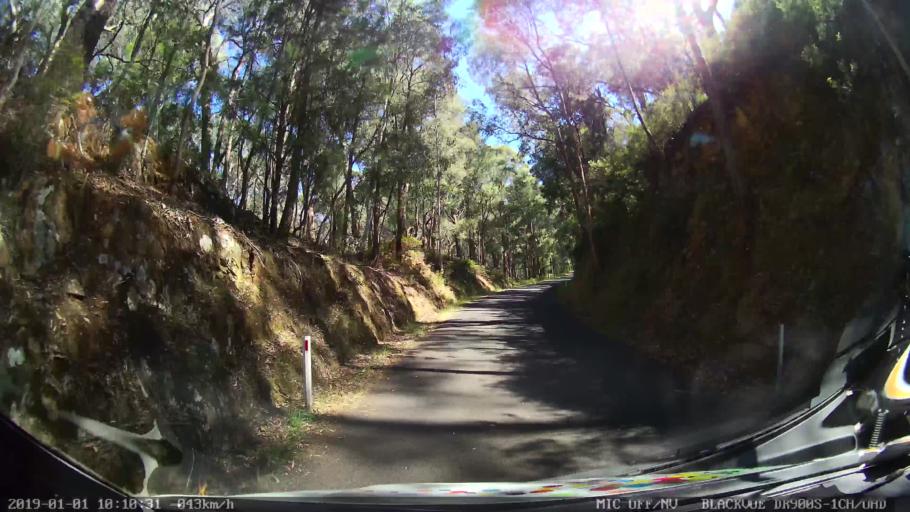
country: AU
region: New South Wales
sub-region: Snowy River
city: Jindabyne
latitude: -36.1407
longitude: 148.1579
